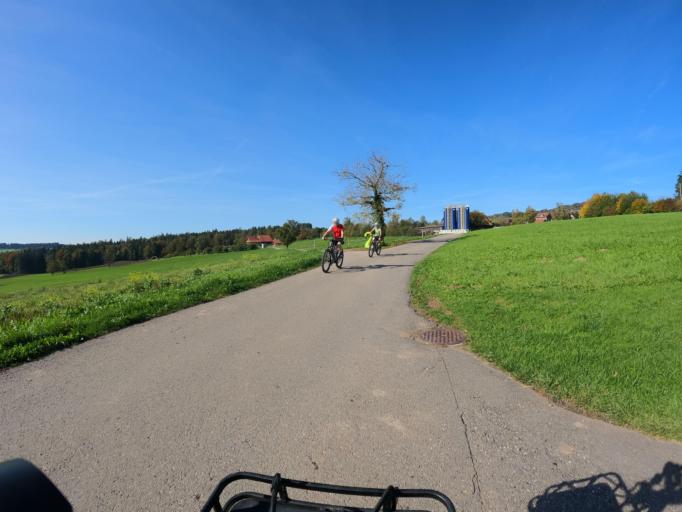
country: CH
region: Zug
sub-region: Zug
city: Baar
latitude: 47.2138
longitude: 8.5563
